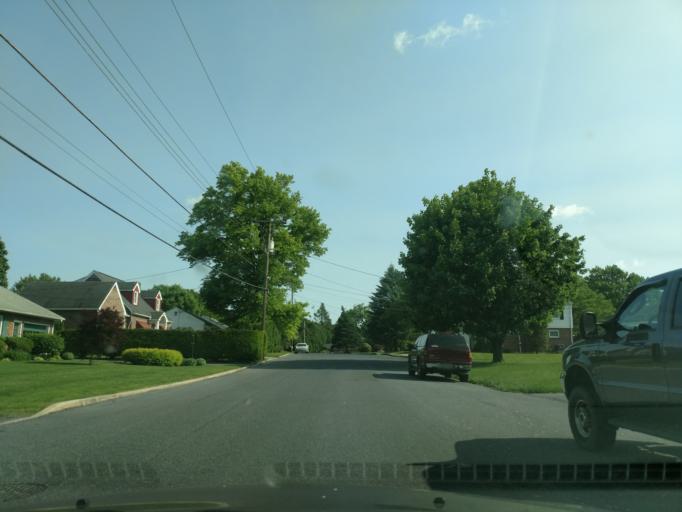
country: US
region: Pennsylvania
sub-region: Lebanon County
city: Lebanon South
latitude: 40.3271
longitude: -76.4097
